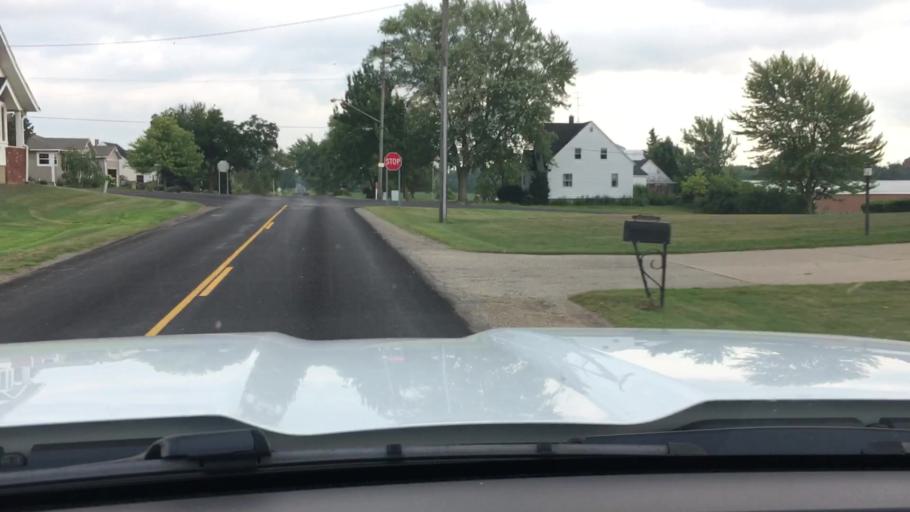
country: US
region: Michigan
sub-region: Ottawa County
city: Hudsonville
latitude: 42.8265
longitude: -85.8817
